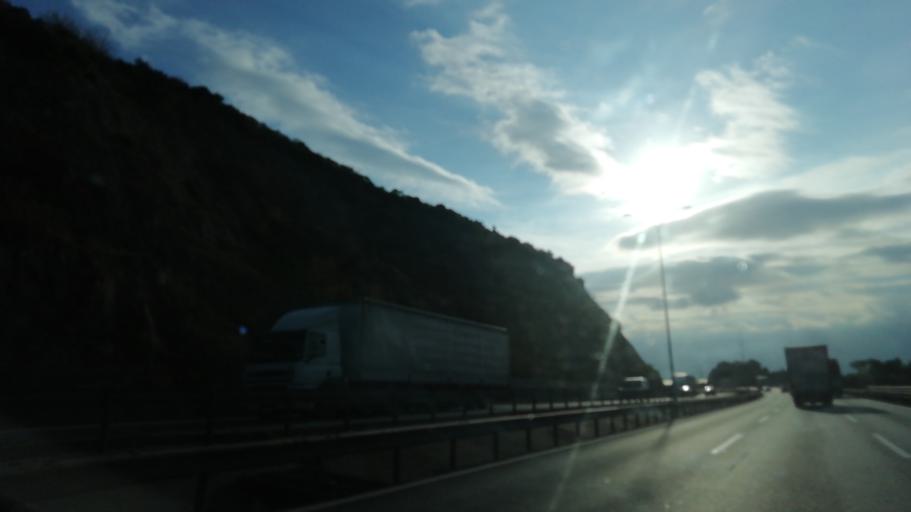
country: TR
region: Kocaeli
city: Hereke
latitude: 40.7805
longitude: 29.6290
